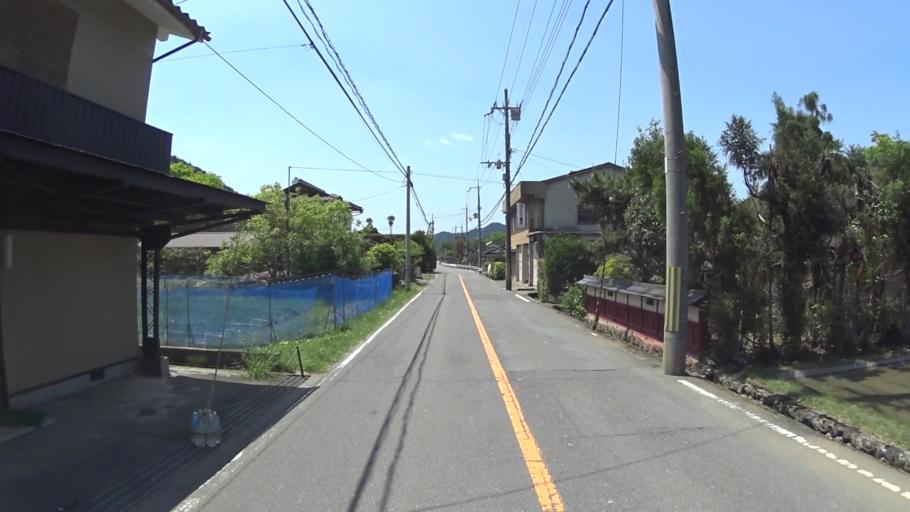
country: JP
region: Kyoto
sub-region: Kyoto-shi
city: Kamigyo-ku
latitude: 35.1782
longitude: 135.6579
